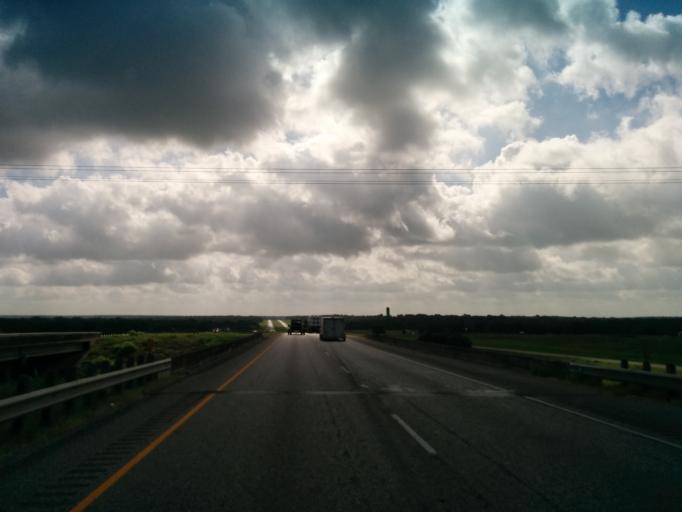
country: US
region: Texas
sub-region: Gonzales County
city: Waelder
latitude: 29.6581
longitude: -97.4159
